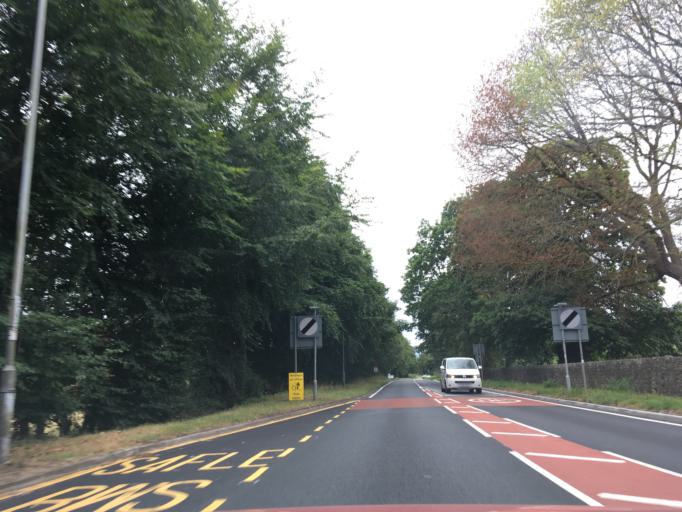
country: GB
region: Wales
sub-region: Monmouthshire
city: Gilwern
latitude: 51.8414
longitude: -3.1109
